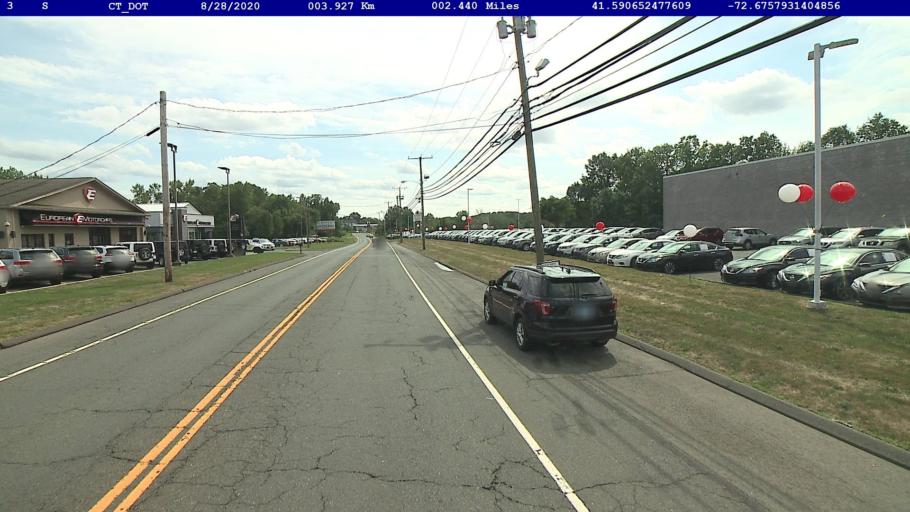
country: US
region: Connecticut
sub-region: Middlesex County
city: Cromwell
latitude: 41.5908
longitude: -72.6758
